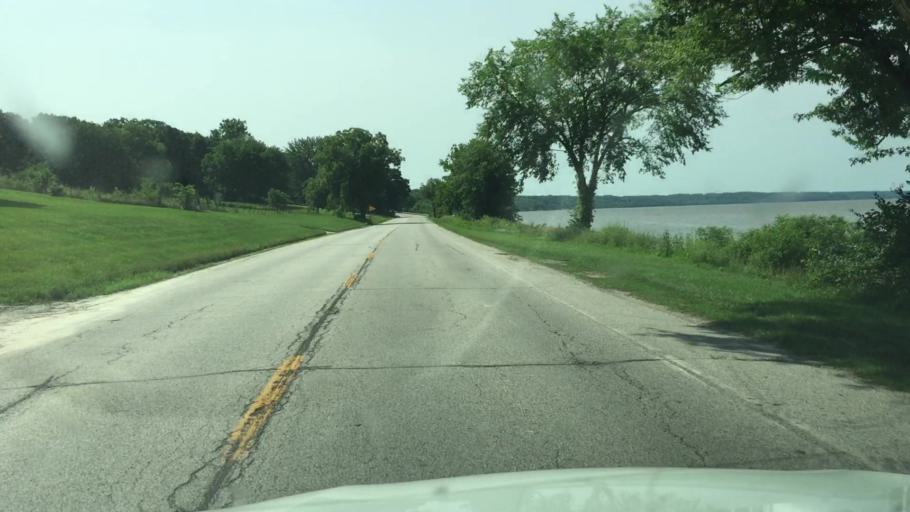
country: US
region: Illinois
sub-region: Hancock County
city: Nauvoo
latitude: 40.5244
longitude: -91.3672
